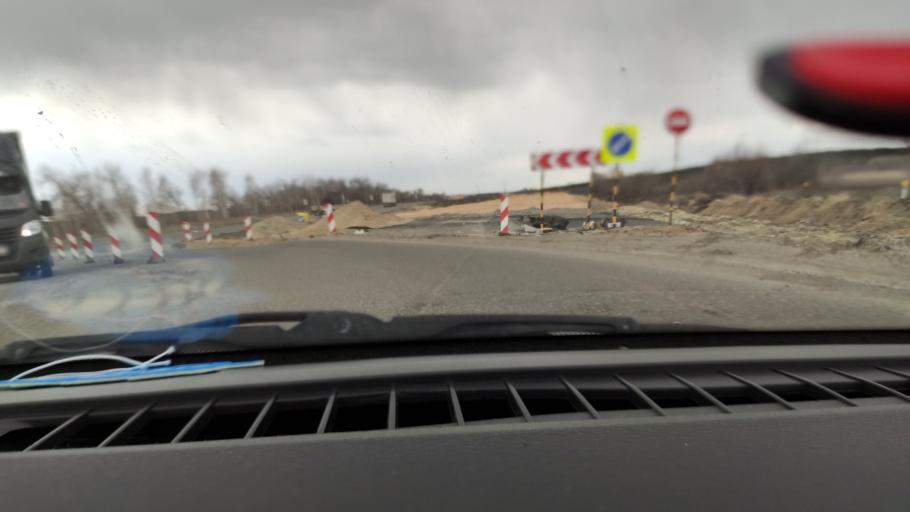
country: RU
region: Saratov
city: Sinodskoye
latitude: 52.0182
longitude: 46.7017
